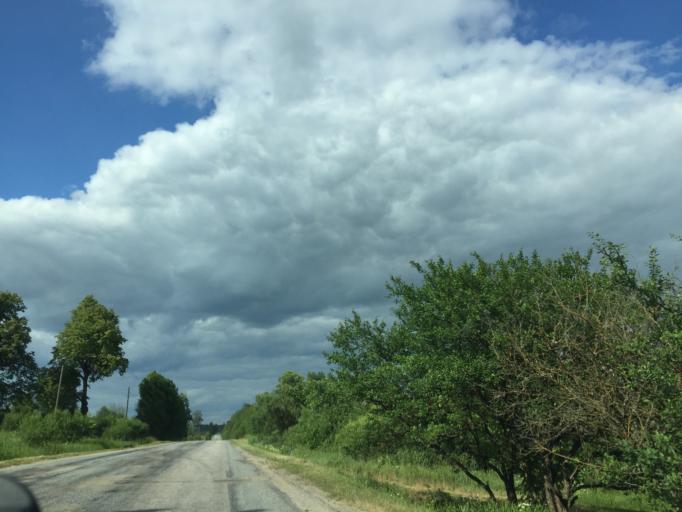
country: LV
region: Skriveri
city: Skriveri
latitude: 56.8108
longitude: 25.1140
